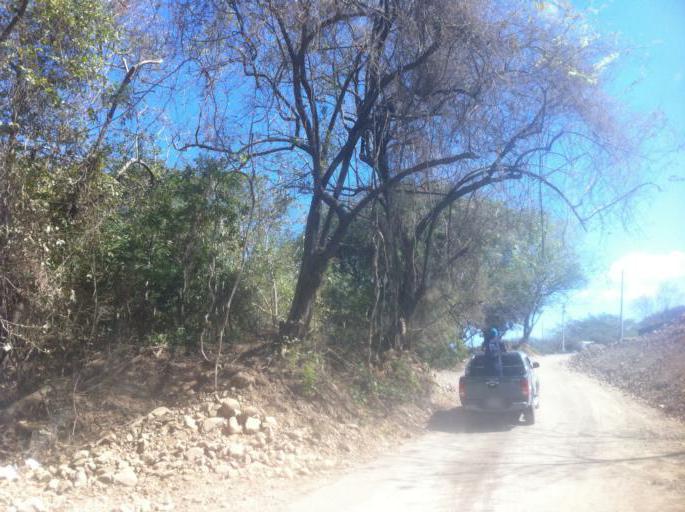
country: NI
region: Rivas
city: Tola
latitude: 11.3977
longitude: -85.9922
